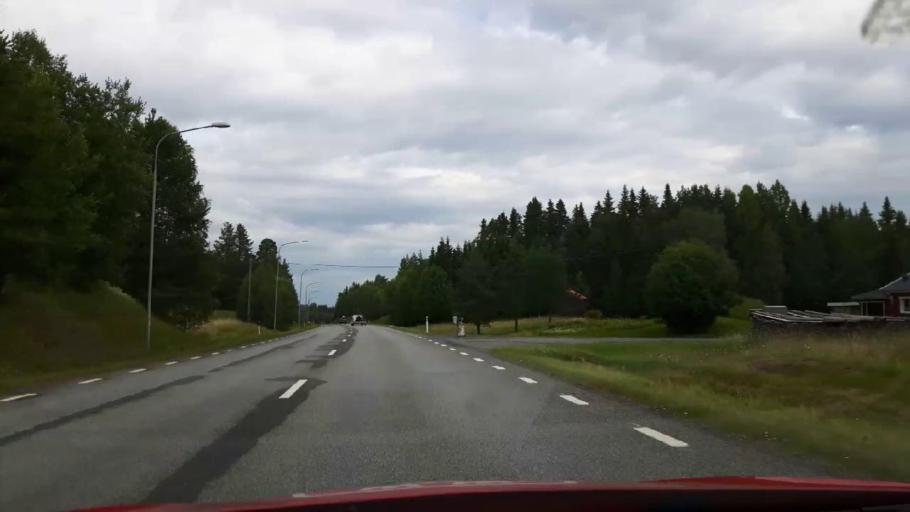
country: SE
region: Jaemtland
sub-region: Stroemsunds Kommun
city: Stroemsund
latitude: 63.6658
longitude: 15.3910
